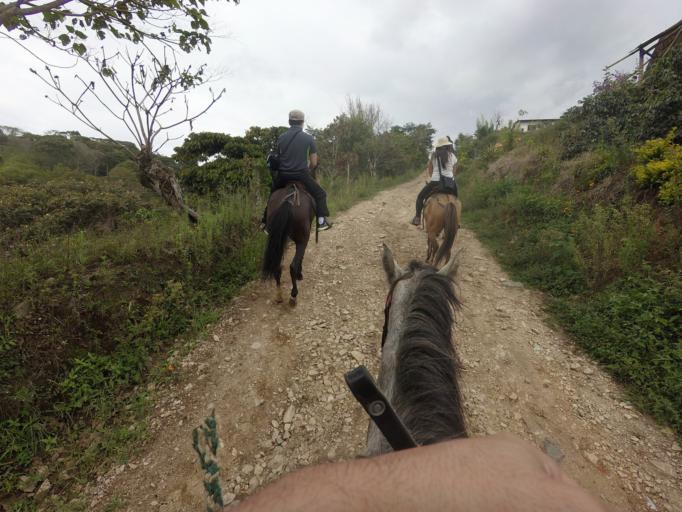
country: CO
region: Huila
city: San Agustin
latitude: 1.8955
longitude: -76.2961
